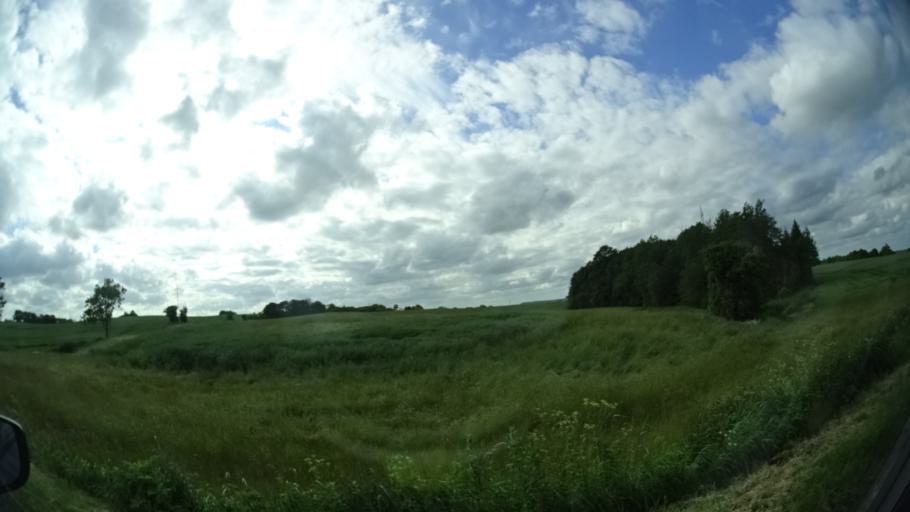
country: DK
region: Central Jutland
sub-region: Syddjurs Kommune
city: Ronde
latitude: 56.3212
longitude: 10.4317
